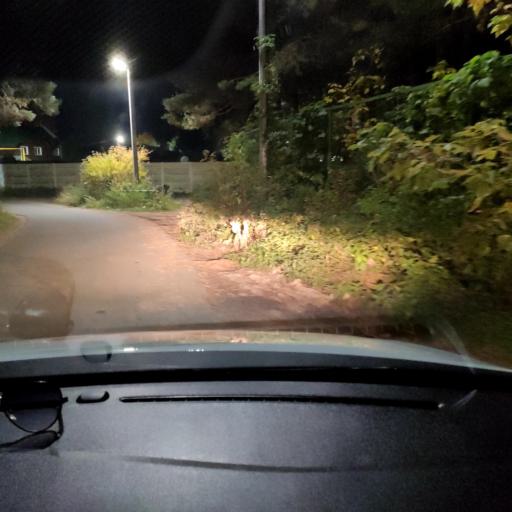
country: RU
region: Tatarstan
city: Verkhniy Uslon
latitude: 55.6226
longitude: 49.0181
